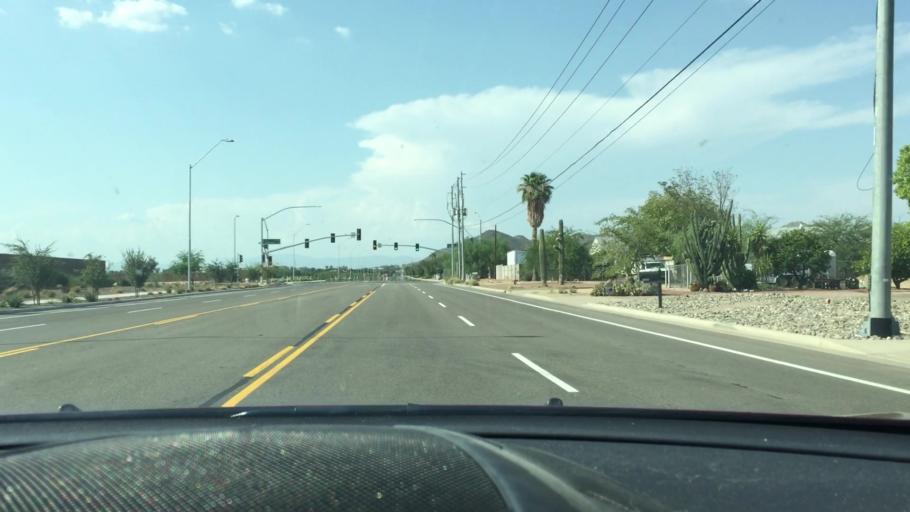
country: US
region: Arizona
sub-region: Maricopa County
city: Sun City West
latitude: 33.6878
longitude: -112.2551
